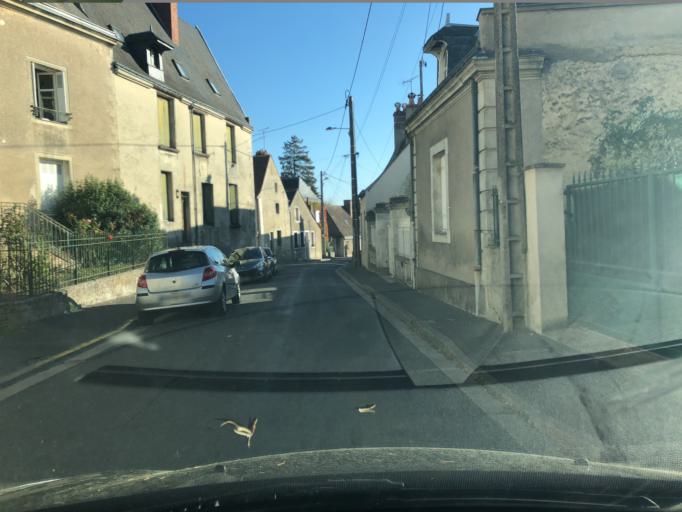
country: FR
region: Centre
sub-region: Departement d'Indre-et-Loire
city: Neuvy-le-Roi
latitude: 47.6032
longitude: 0.5955
